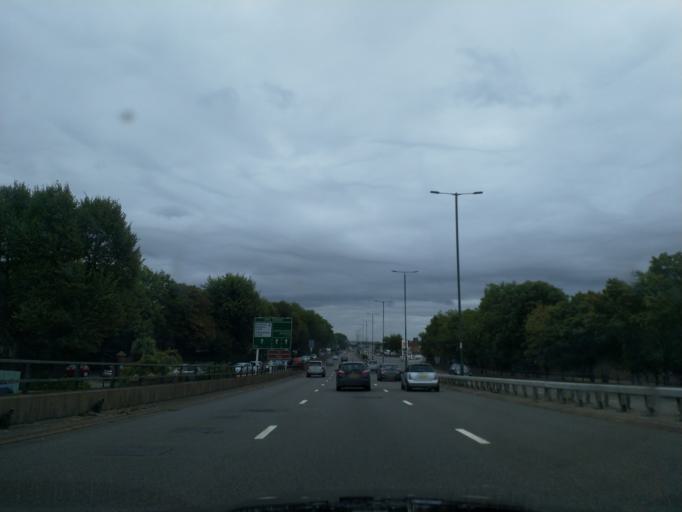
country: GB
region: England
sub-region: Greater London
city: Feltham
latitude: 51.4338
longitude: -0.3909
